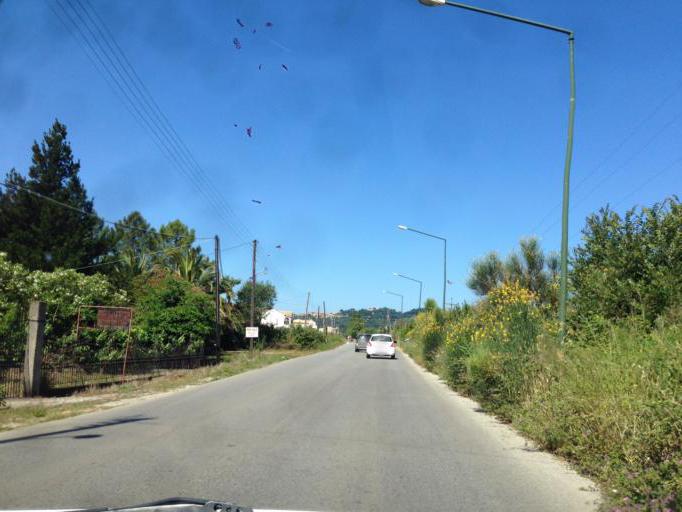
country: GR
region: Ionian Islands
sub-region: Nomos Kerkyras
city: Acharavi
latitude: 39.7861
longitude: 19.7801
